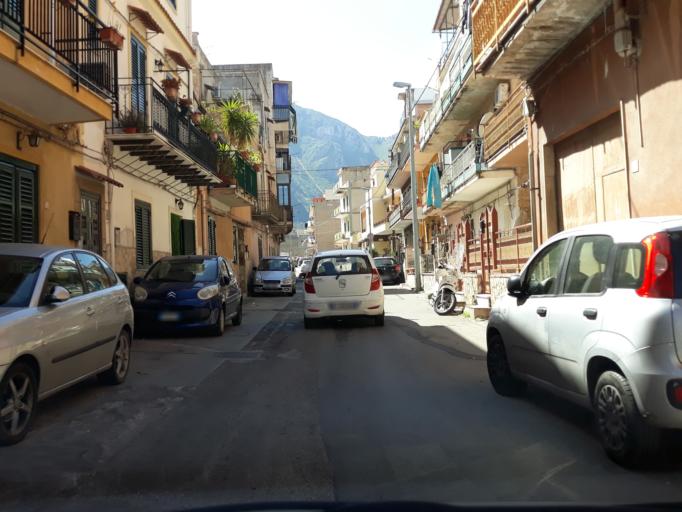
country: IT
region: Sicily
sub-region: Palermo
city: Ciaculli
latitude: 38.0813
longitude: 13.3742
